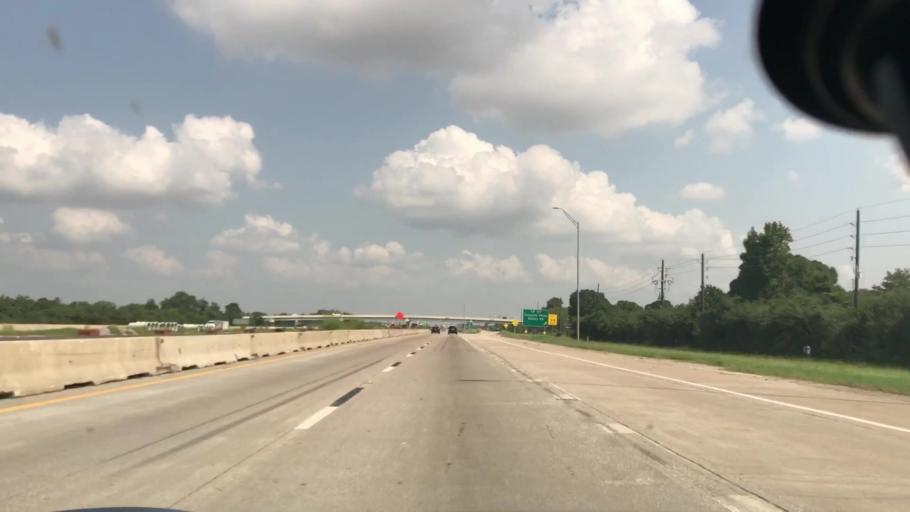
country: US
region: Texas
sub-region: Brazoria County
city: Iowa Colony
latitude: 29.5210
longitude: -95.3862
